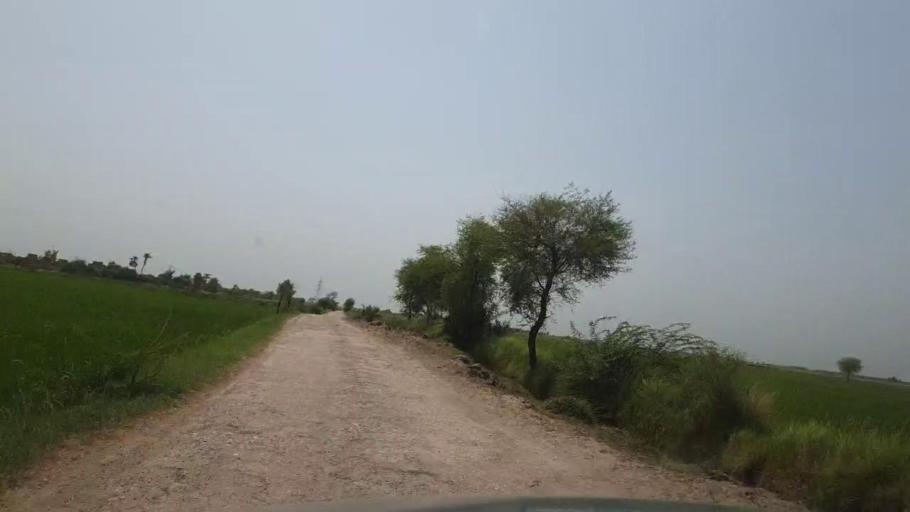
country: PK
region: Sindh
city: Garhi Yasin
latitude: 27.8959
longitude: 68.4849
